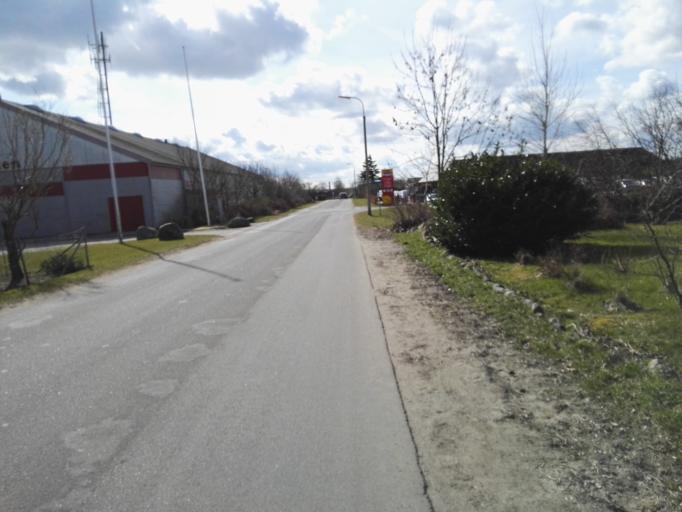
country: DK
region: Zealand
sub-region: Lejre Kommune
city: Ejby
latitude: 55.7649
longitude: 11.8049
